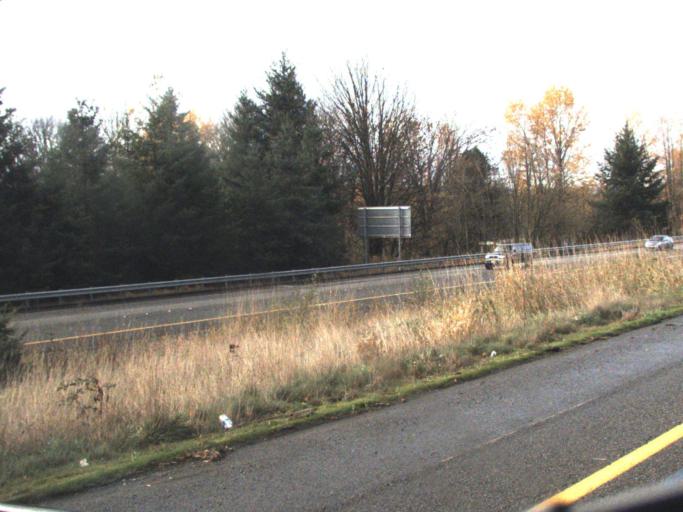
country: US
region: Washington
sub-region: Snohomish County
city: Fobes Hill
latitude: 47.9639
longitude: -122.1260
